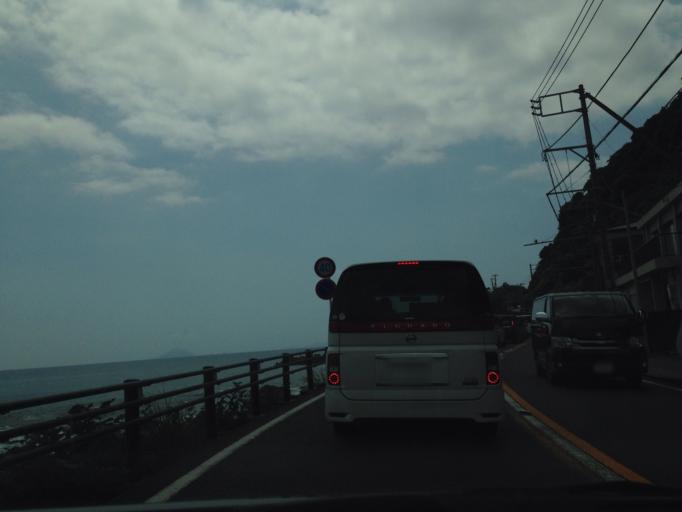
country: JP
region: Shizuoka
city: Shimoda
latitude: 34.7411
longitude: 138.9985
